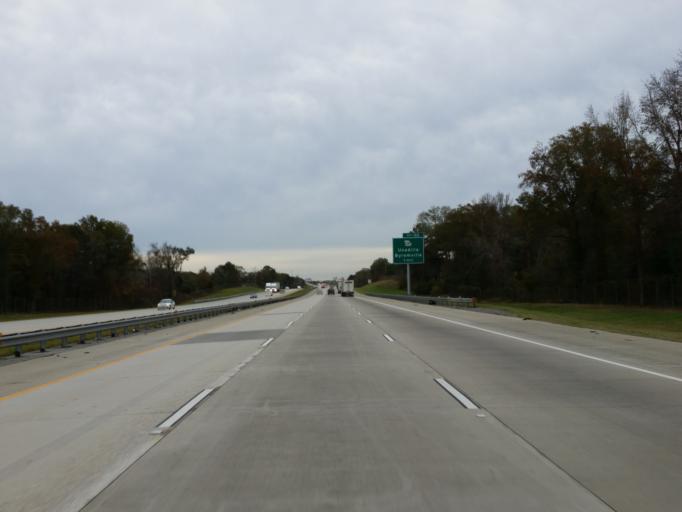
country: US
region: Georgia
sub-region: Dooly County
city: Unadilla
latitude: 32.2780
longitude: -83.7552
